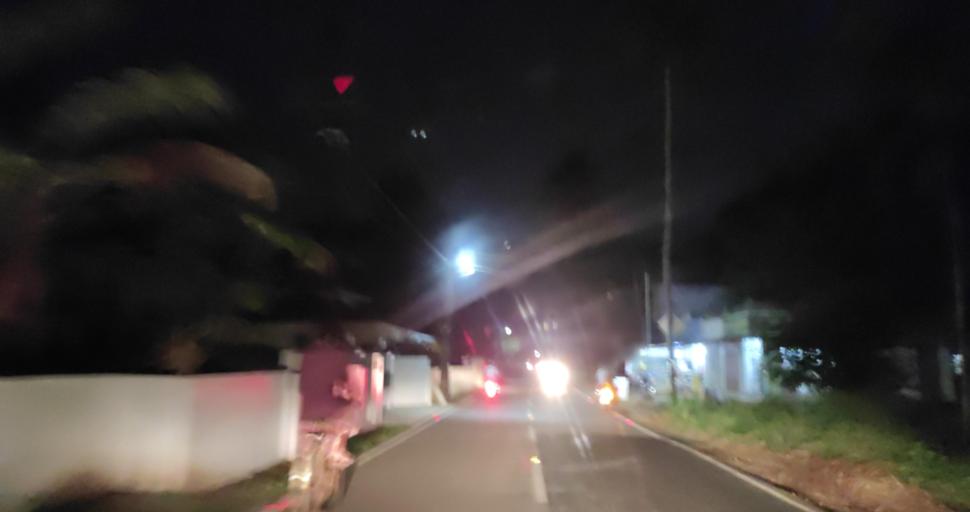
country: IN
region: Kerala
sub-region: Alappuzha
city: Vayalar
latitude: 9.6808
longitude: 76.3209
